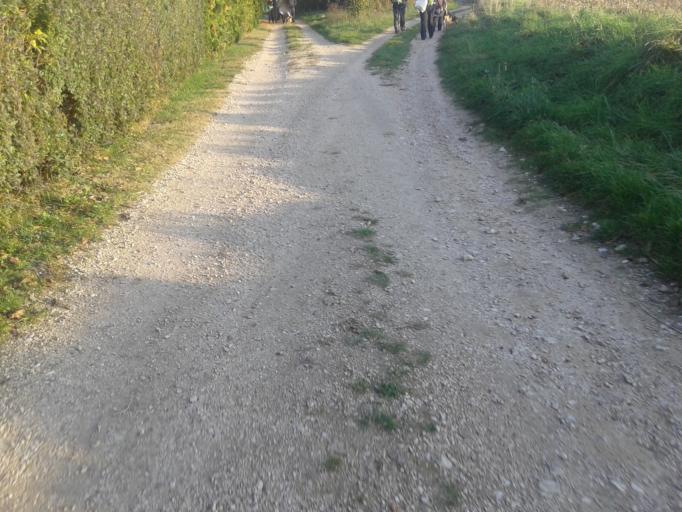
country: HU
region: Fejer
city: Fehervarcsurgo
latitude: 47.2911
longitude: 18.2534
